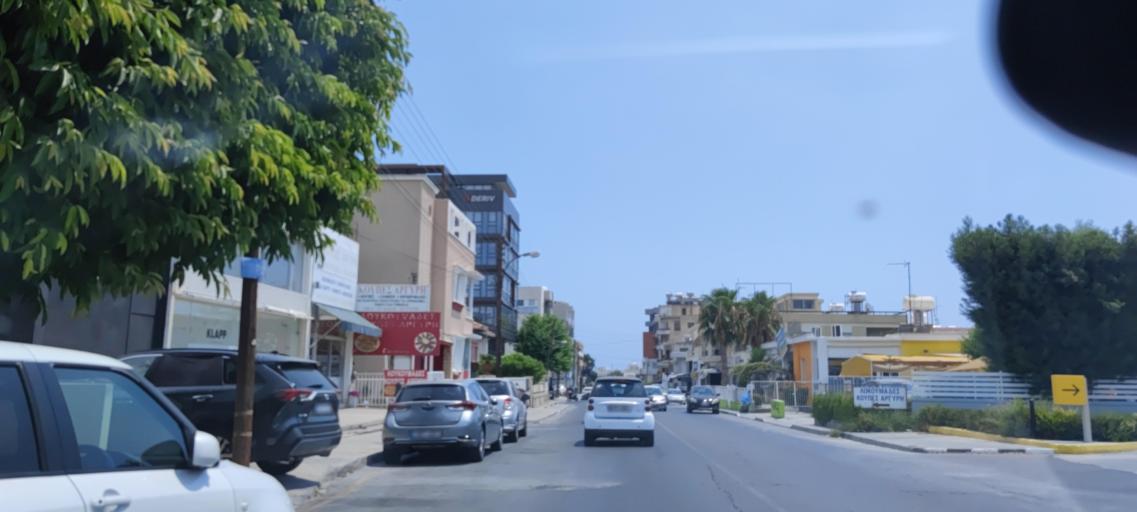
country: CY
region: Limassol
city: Limassol
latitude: 34.6814
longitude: 33.0391
